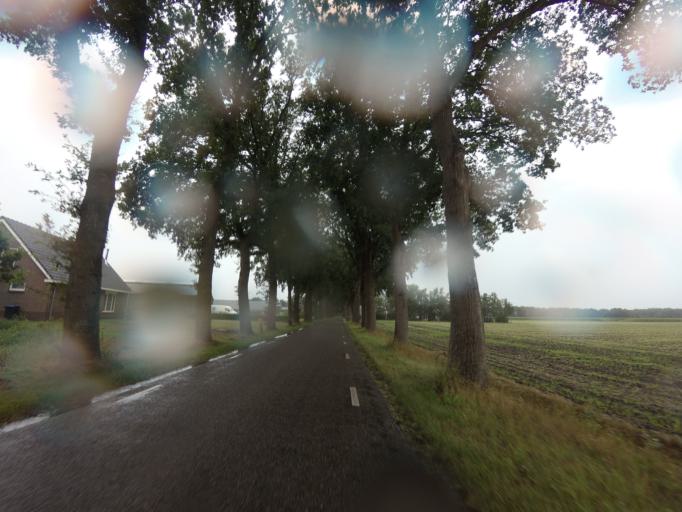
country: NL
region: Drenthe
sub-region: Gemeente Hoogeveen
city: Hoogeveen
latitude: 52.6489
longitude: 6.4732
